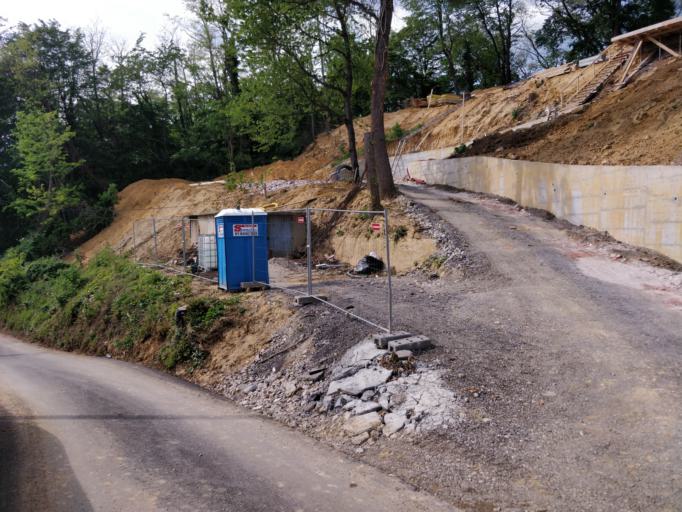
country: HR
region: Grad Zagreb
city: Zagreb
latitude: 45.8506
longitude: 15.9791
